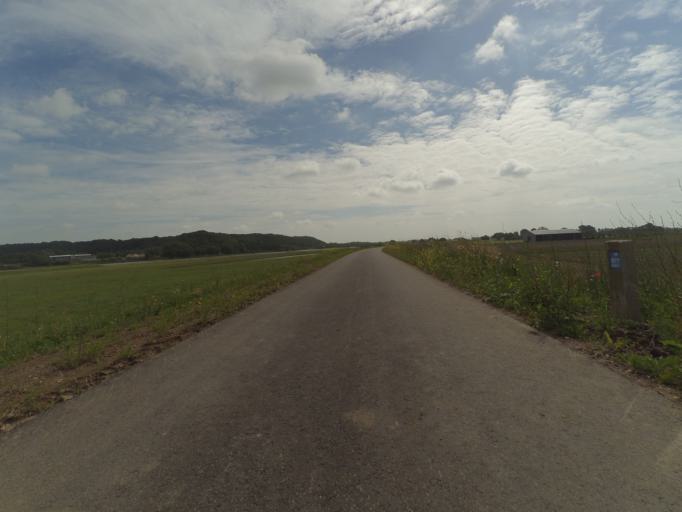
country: NL
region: Utrecht
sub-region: Gemeente Rhenen
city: Rhenen
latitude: 51.9485
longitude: 5.5793
